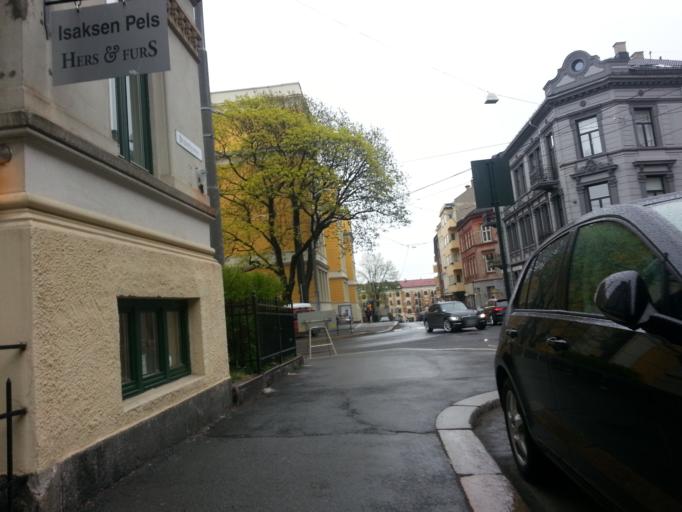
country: NO
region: Oslo
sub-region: Oslo
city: Oslo
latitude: 59.9206
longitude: 10.7172
